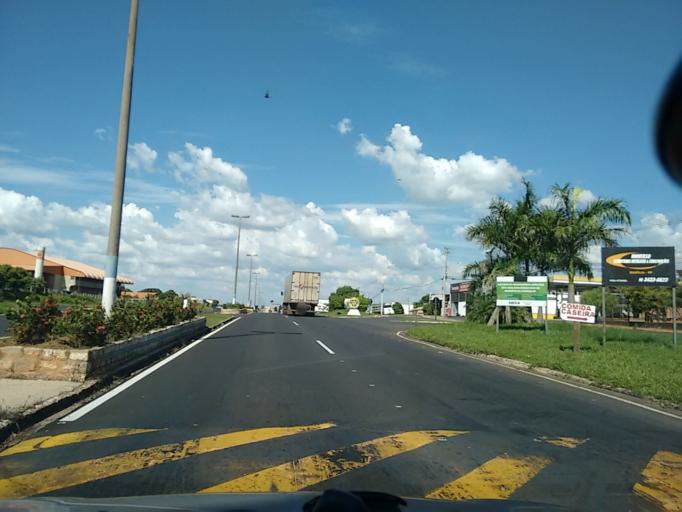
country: BR
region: Sao Paulo
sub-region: Pompeia
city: Pompeia
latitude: -22.1043
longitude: -50.1930
